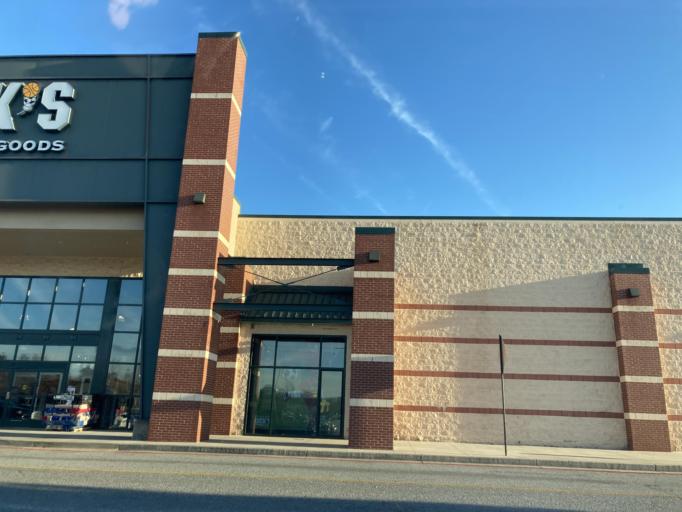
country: US
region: Georgia
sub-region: Bibb County
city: Macon
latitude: 32.9246
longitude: -83.7134
